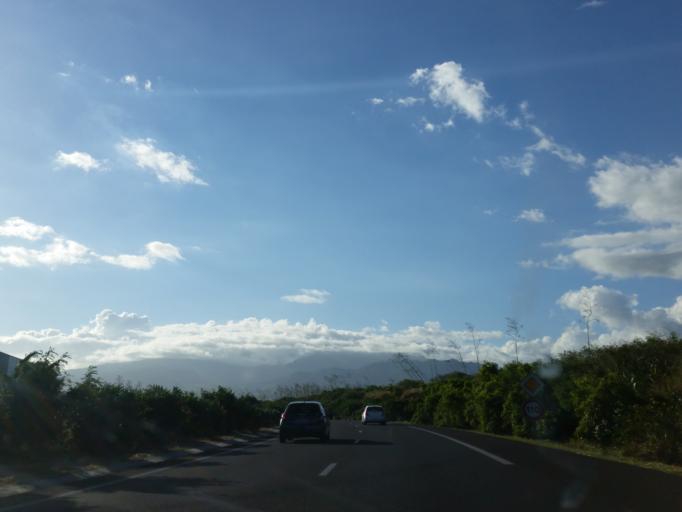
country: RE
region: Reunion
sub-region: Reunion
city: Saint-Pierre
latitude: -21.3208
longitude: 55.4464
